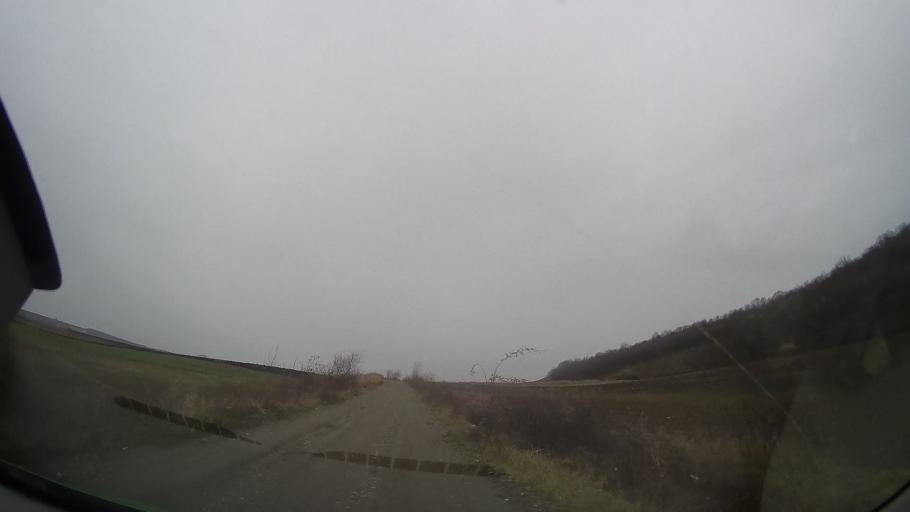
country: RO
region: Mures
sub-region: Comuna Ceausu de Campie
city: Ceausu de Campie
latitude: 46.6523
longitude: 24.4968
